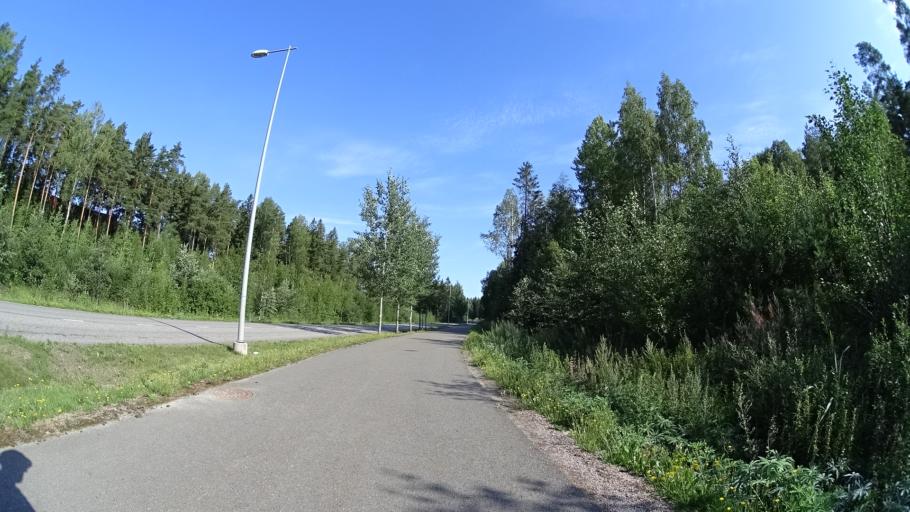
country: FI
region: Uusimaa
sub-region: Helsinki
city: Kilo
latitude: 60.2838
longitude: 24.7622
